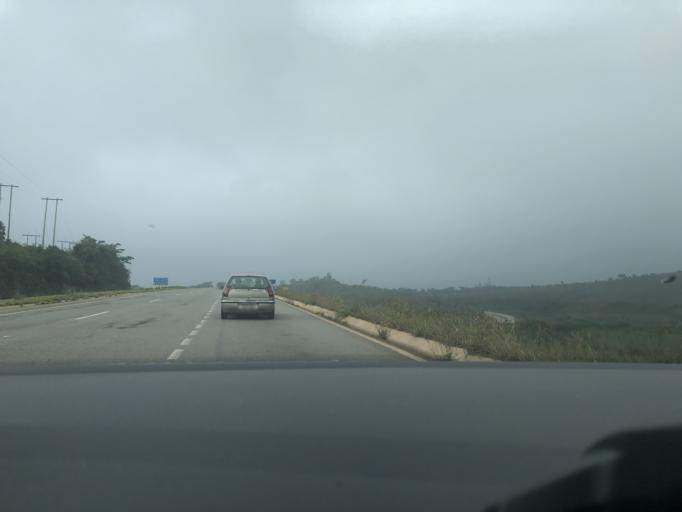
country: BR
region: Minas Gerais
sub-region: Congonhas
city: Congonhas
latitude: -20.5857
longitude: -43.9454
